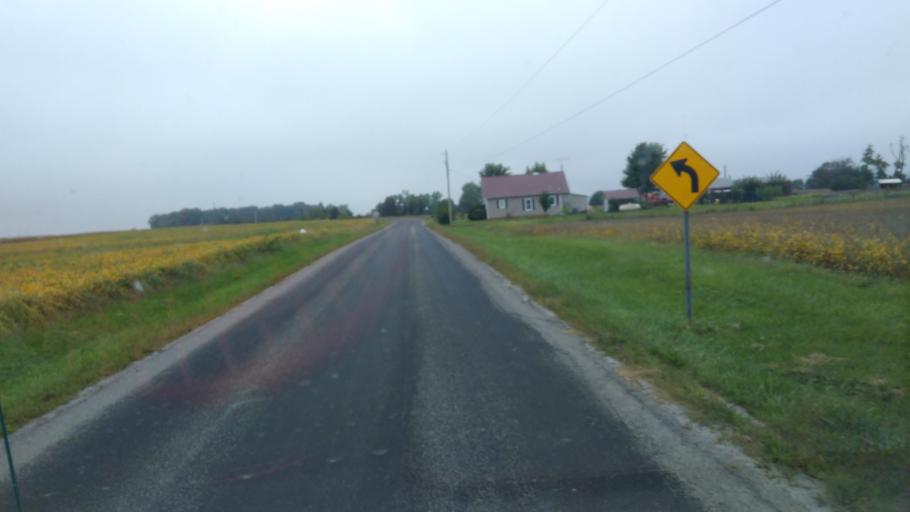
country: US
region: Ohio
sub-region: Logan County
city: Northwood
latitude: 40.5240
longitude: -83.6253
